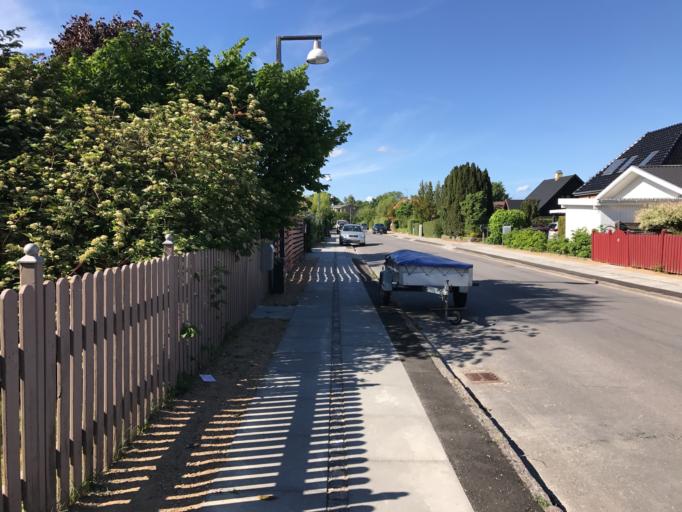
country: DK
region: Capital Region
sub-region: Hvidovre Kommune
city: Hvidovre
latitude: 55.6685
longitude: 12.4710
